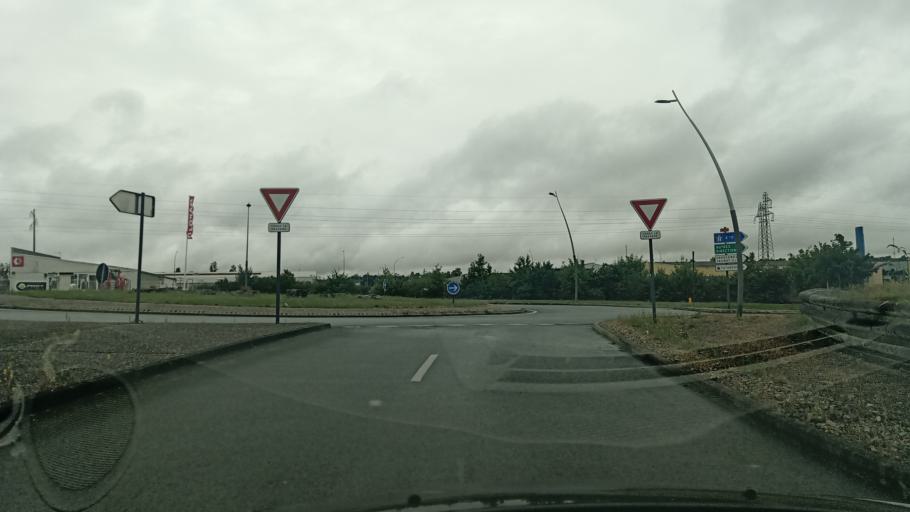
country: FR
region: Poitou-Charentes
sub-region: Departement de la Vienne
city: Poitiers
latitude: 46.6129
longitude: 0.3480
